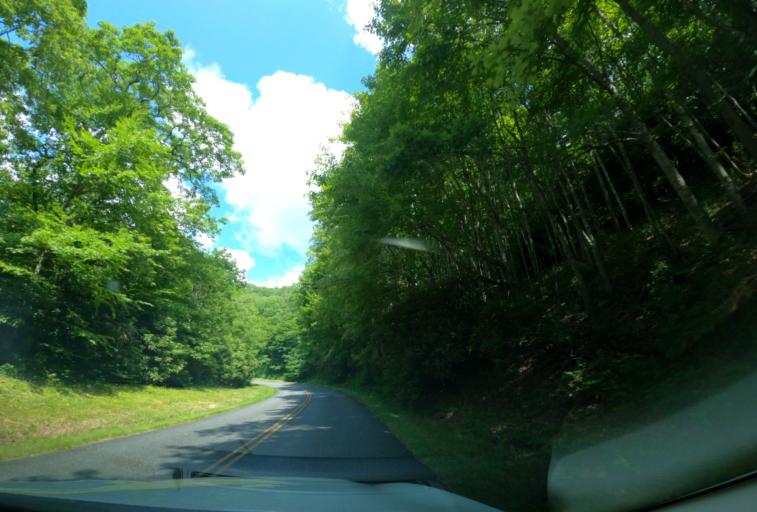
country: US
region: North Carolina
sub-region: Haywood County
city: Maggie Valley
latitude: 35.4500
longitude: -83.1104
